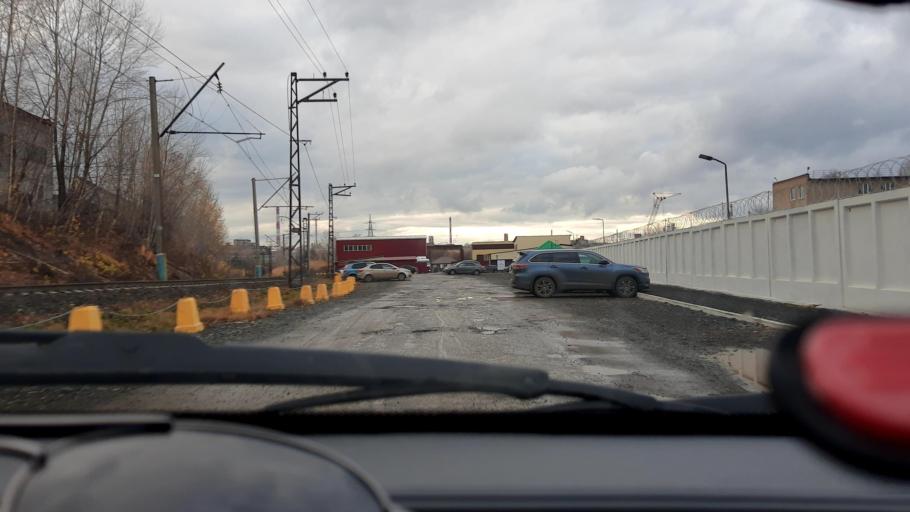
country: RU
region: Bashkortostan
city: Ufa
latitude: 54.8360
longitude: 56.1139
